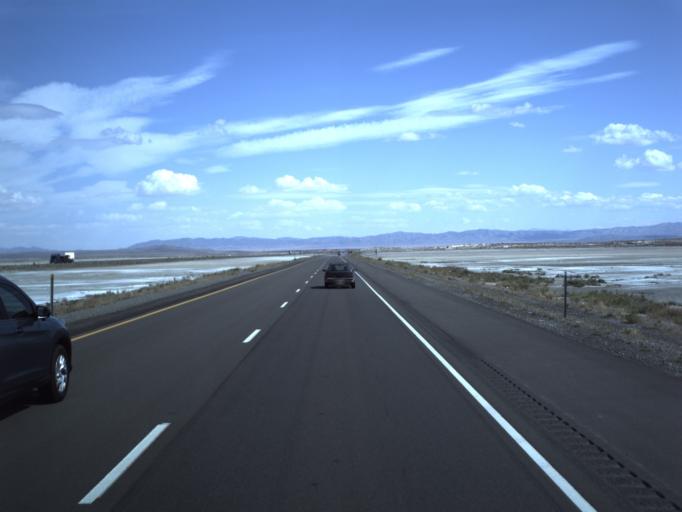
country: US
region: Utah
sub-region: Tooele County
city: Wendover
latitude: 40.7272
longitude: -113.3046
